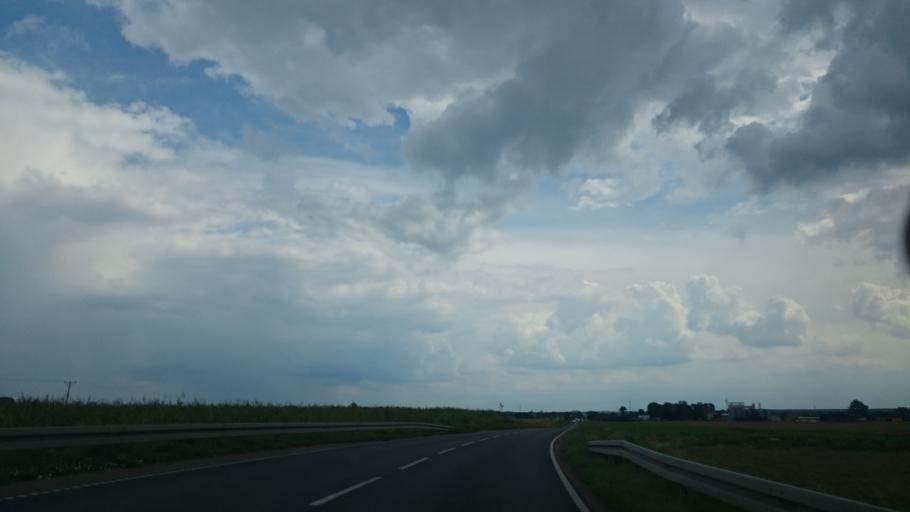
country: PL
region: Kujawsko-Pomorskie
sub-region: Powiat tucholski
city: Kesowo
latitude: 53.6604
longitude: 17.6819
